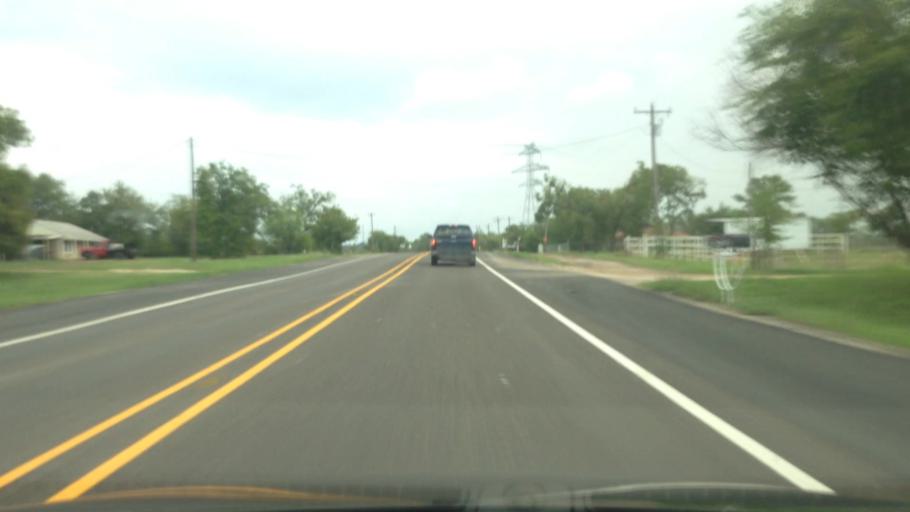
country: US
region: Texas
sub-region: Johnson County
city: Burleson
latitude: 32.5101
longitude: -97.3459
